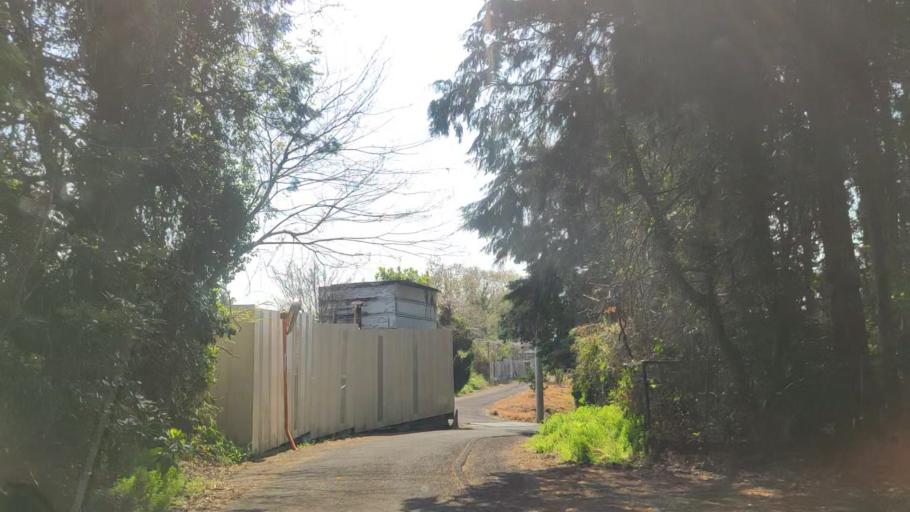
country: JP
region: Kanagawa
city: Ninomiya
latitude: 35.3243
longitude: 139.2708
